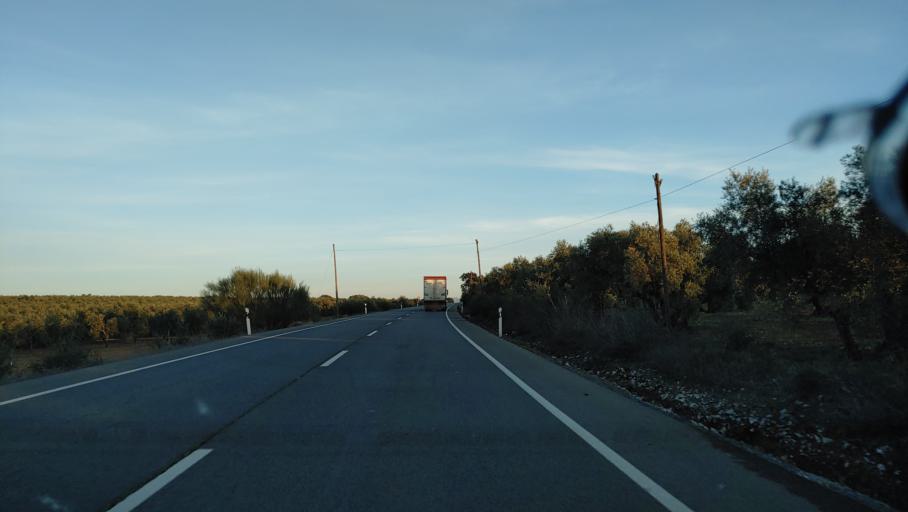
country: ES
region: Andalusia
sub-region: Provincia de Malaga
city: Humilladero
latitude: 37.0581
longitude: -4.6808
